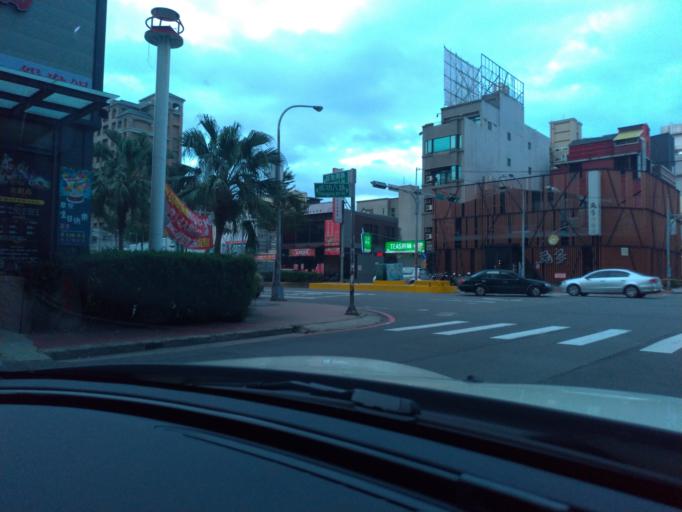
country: TW
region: Taiwan
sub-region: Hsinchu
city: Zhubei
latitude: 24.8168
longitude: 121.0200
